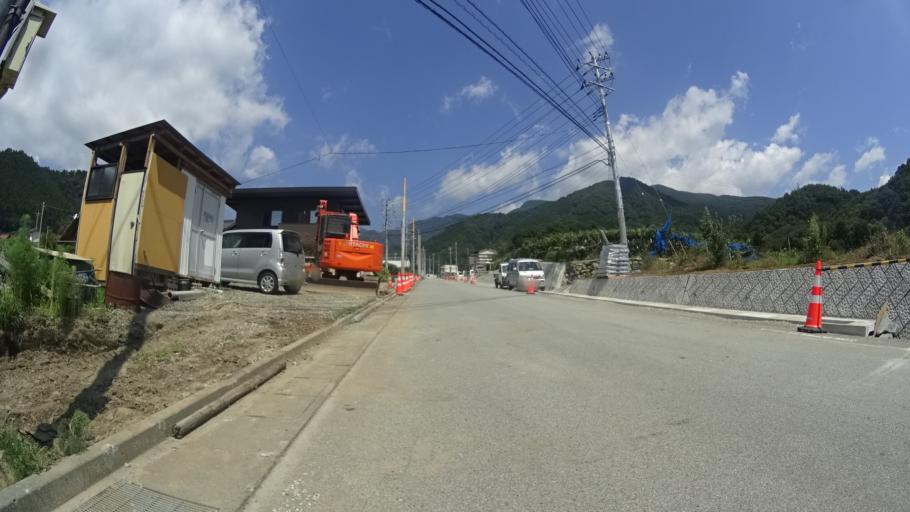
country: JP
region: Yamanashi
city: Enzan
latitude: 35.7664
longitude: 138.7042
